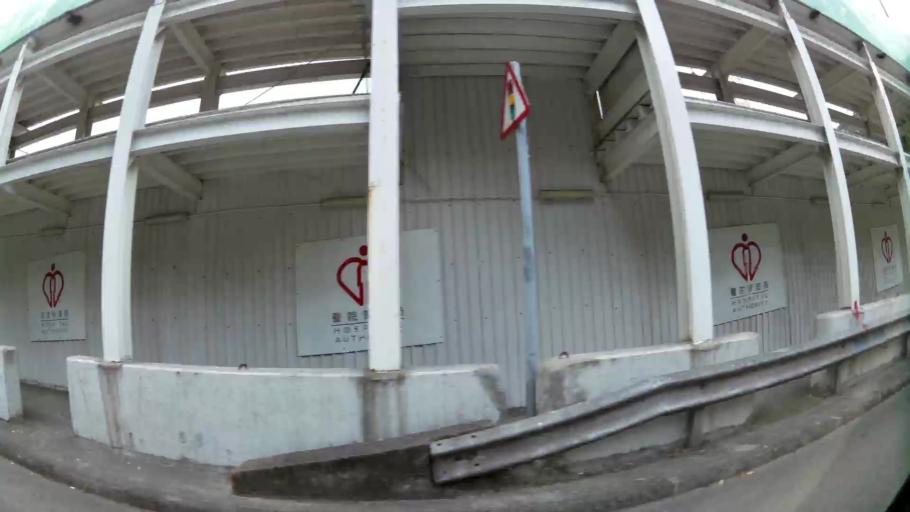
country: HK
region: Kowloon City
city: Kowloon
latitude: 22.3238
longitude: 114.2266
